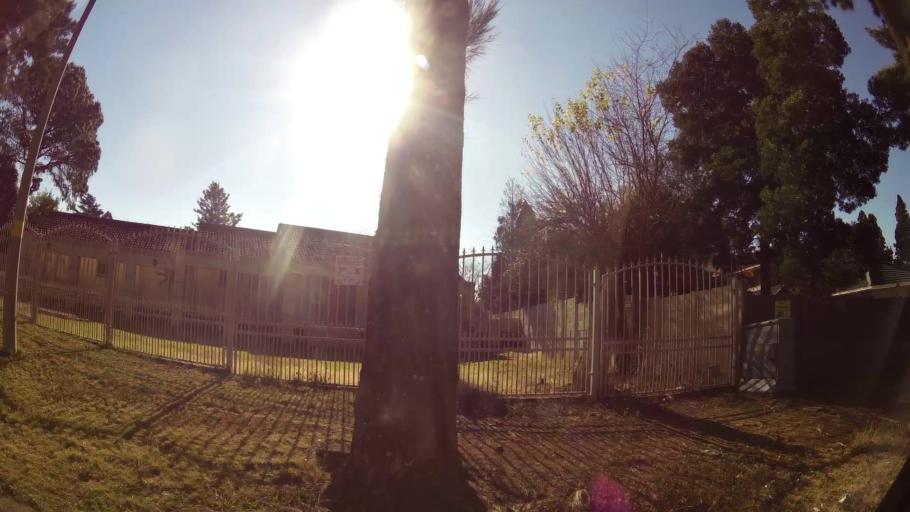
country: ZA
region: Gauteng
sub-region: Ekurhuleni Metropolitan Municipality
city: Germiston
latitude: -26.3365
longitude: 28.1020
